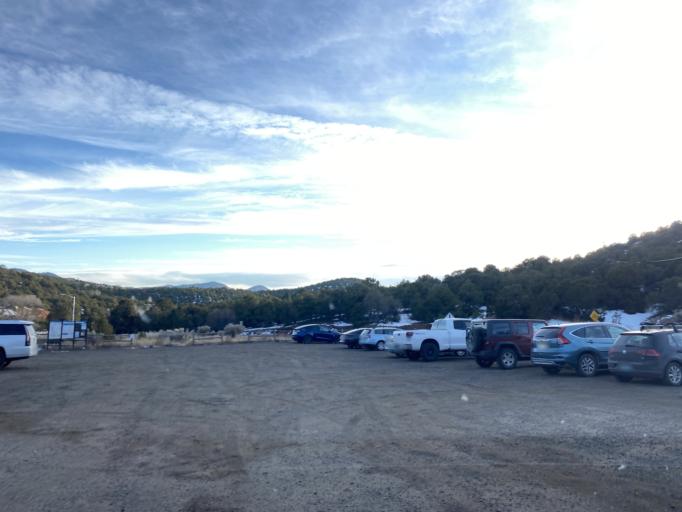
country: US
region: New Mexico
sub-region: Santa Fe County
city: Santa Fe
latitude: 35.7108
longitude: -105.8994
